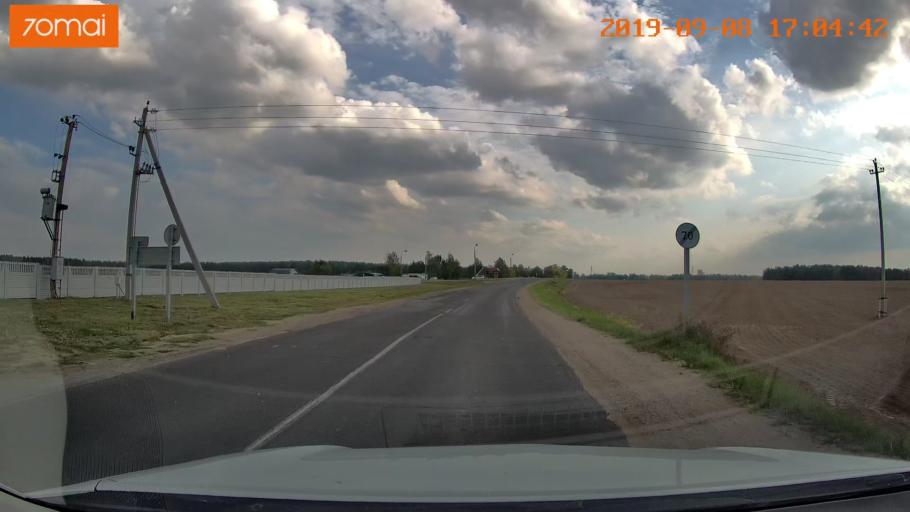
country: BY
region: Grodnenskaya
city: Hrodna
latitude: 53.6874
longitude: 23.9552
